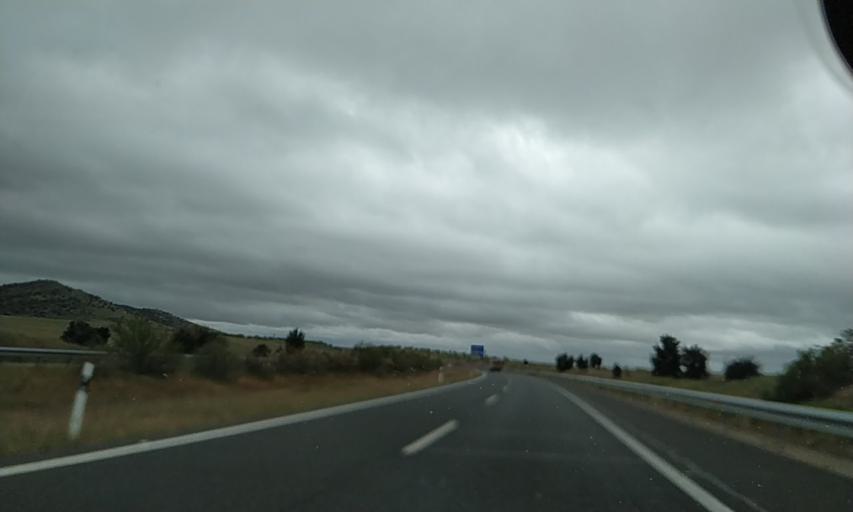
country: ES
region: Extremadura
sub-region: Provincia de Caceres
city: Caceres
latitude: 39.4424
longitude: -6.4129
